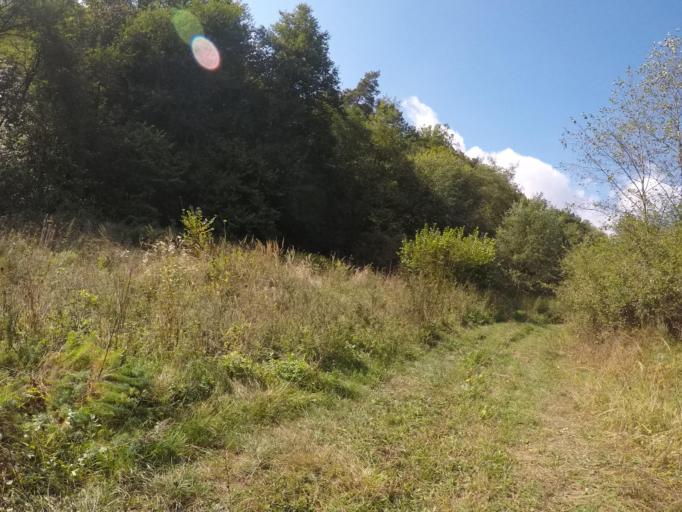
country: SK
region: Presovsky
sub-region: Okres Presov
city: Presov
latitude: 48.9337
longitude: 21.1628
